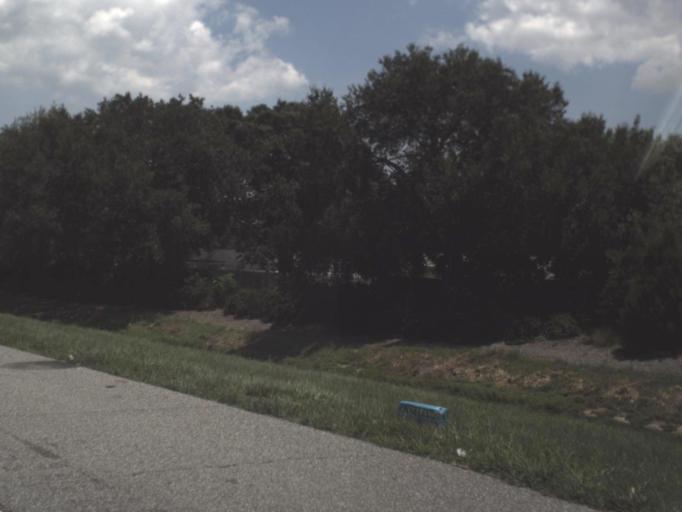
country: US
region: Florida
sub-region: Pinellas County
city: Lealman
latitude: 27.8356
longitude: -82.6641
